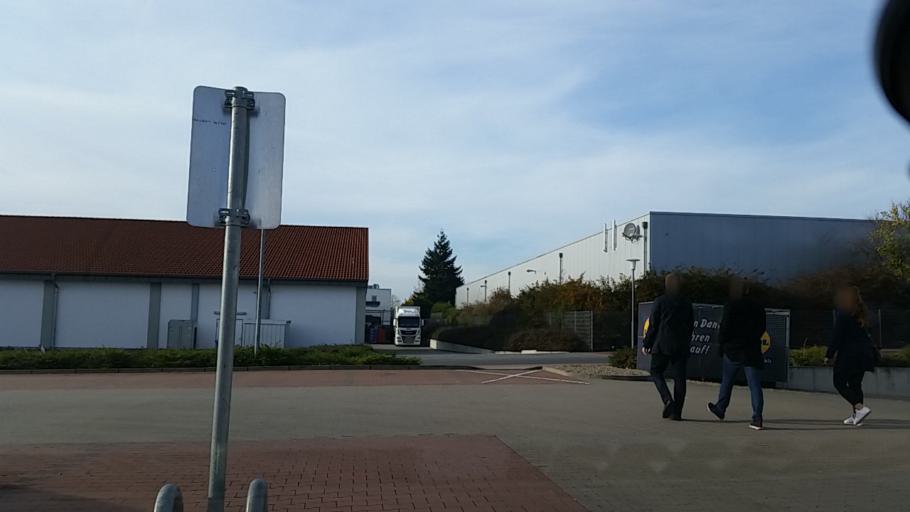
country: DE
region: Lower Saxony
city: Weyhausen
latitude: 52.4633
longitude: 10.7231
